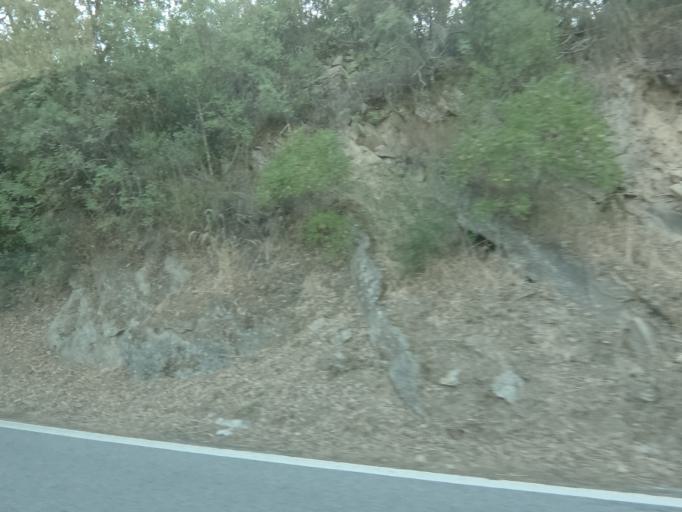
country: PT
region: Viseu
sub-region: Tabuaco
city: Tabuaco
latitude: 41.1230
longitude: -7.5720
